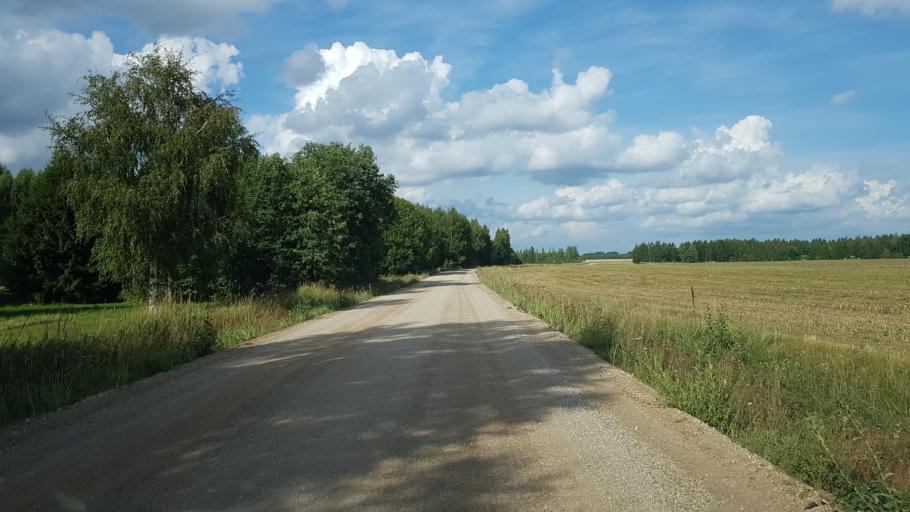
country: RU
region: Pskov
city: Pechory
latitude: 57.7854
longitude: 27.4732
